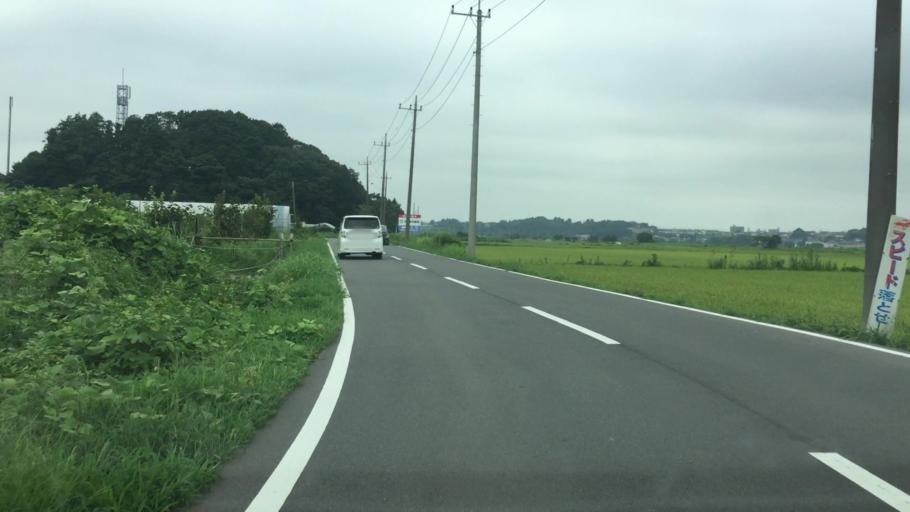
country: JP
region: Chiba
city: Abiko
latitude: 35.8499
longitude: 140.0475
